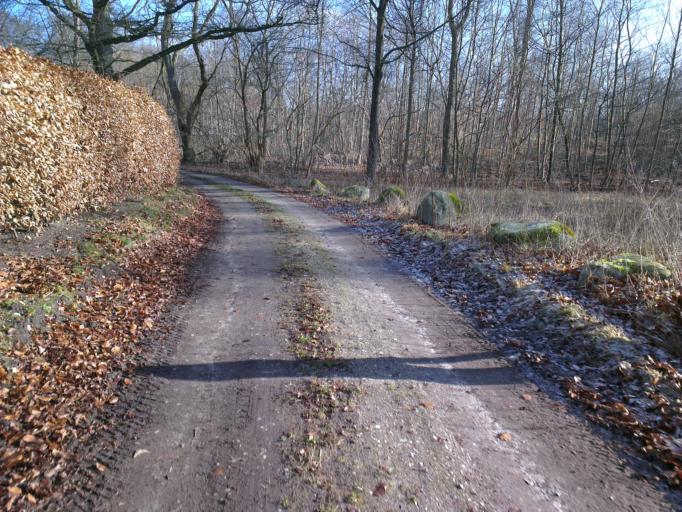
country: DK
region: Capital Region
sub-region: Frederikssund Kommune
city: Jaegerspris
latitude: 55.8999
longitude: 12.0182
